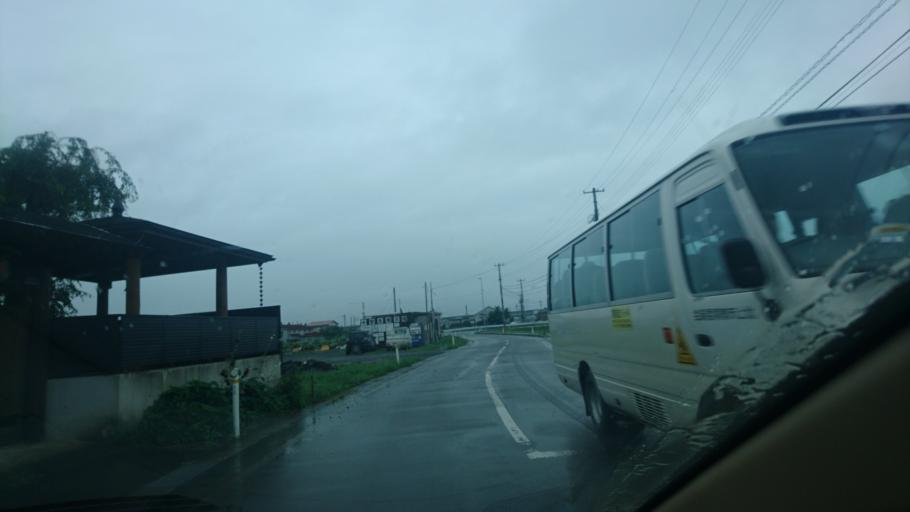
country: JP
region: Iwate
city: Kitakami
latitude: 39.2401
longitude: 141.1210
